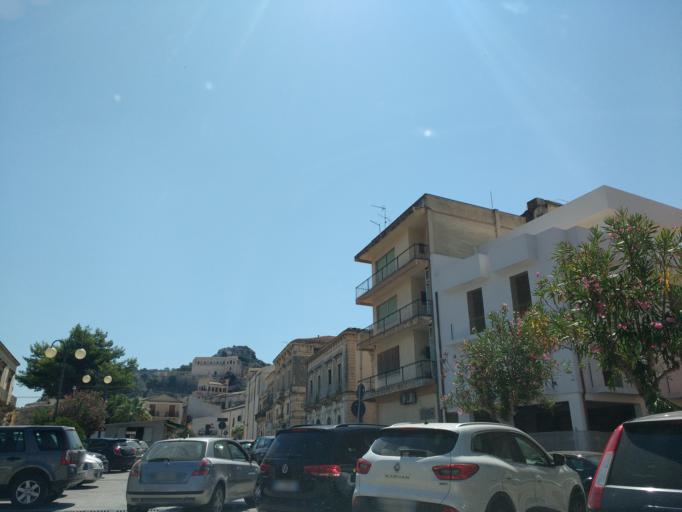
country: IT
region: Sicily
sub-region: Ragusa
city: Scicli
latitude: 36.7939
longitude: 14.7032
